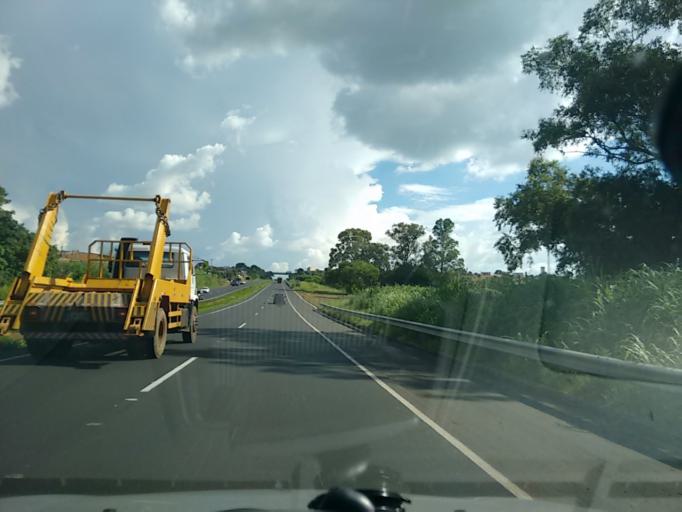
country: BR
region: Sao Paulo
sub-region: Marilia
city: Marilia
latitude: -22.2166
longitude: -49.9650
